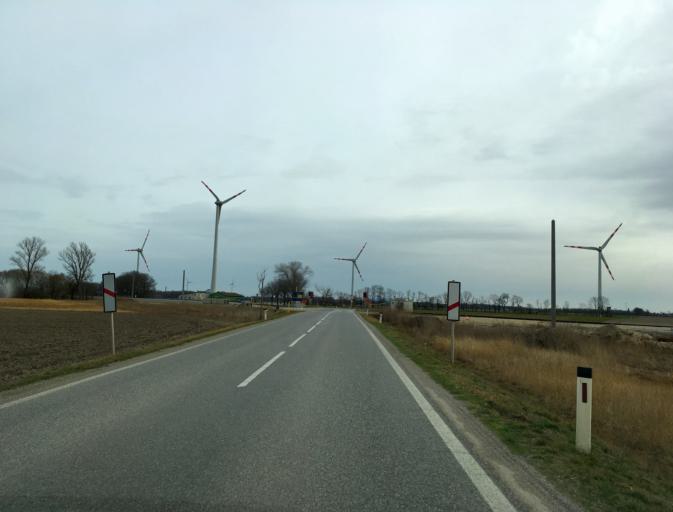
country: AT
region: Lower Austria
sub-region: Politischer Bezirk Ganserndorf
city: Glinzendorf
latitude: 48.2438
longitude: 16.6606
